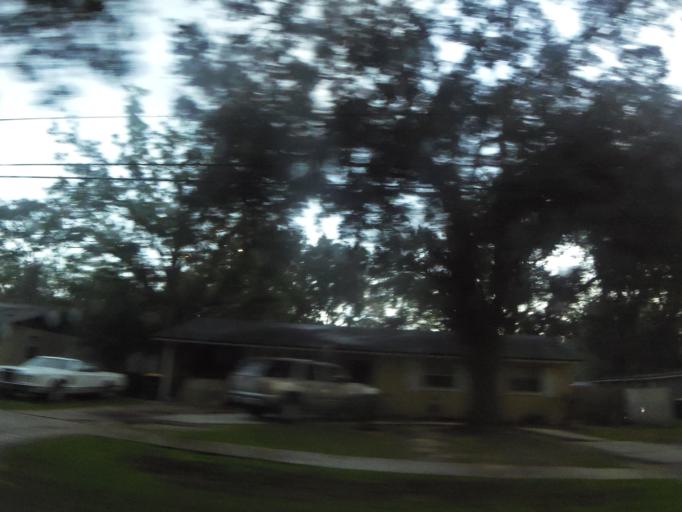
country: US
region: Florida
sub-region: Duval County
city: Jacksonville
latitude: 30.2471
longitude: -81.6187
